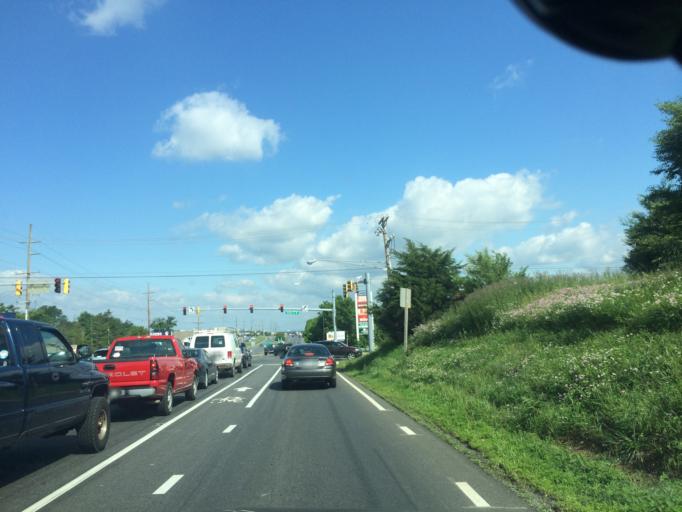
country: US
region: Maryland
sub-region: Carroll County
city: Westminster
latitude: 39.5605
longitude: -76.9674
